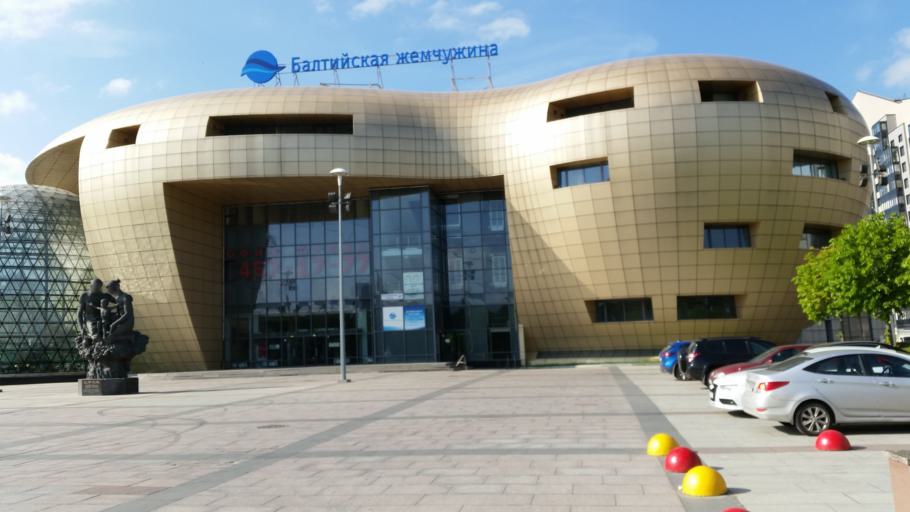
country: RU
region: St.-Petersburg
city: Sosnovaya Polyana
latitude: 59.8480
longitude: 30.1492
